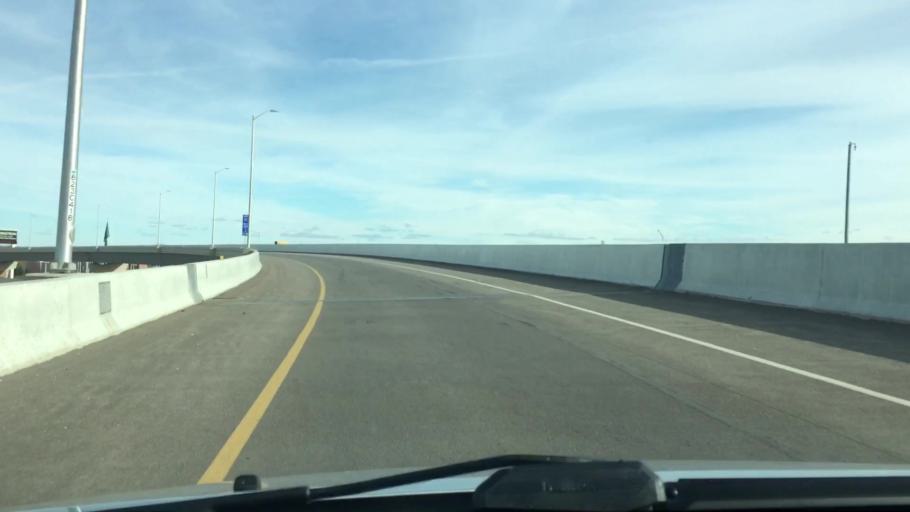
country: US
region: Wisconsin
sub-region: Brown County
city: Howard
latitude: 44.5393
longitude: -88.0789
